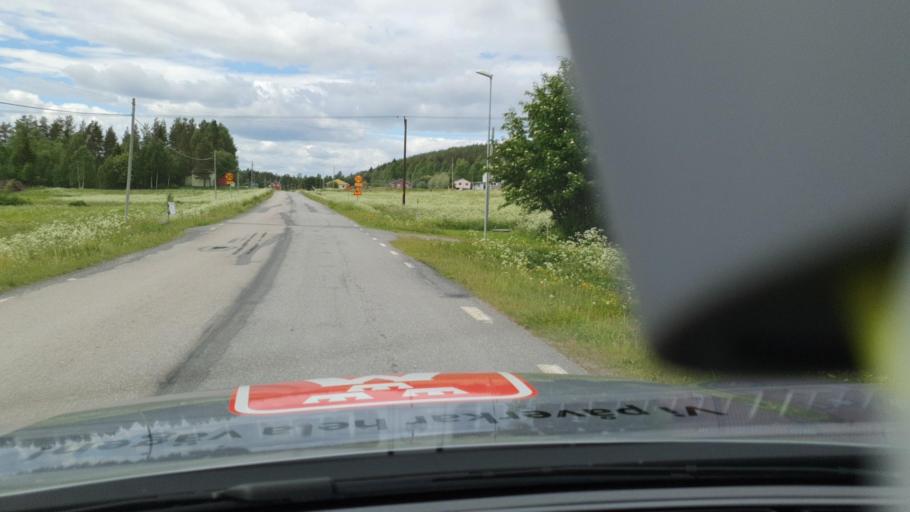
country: SE
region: Norrbotten
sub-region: Bodens Kommun
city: Saevast
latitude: 65.8709
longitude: 21.8916
